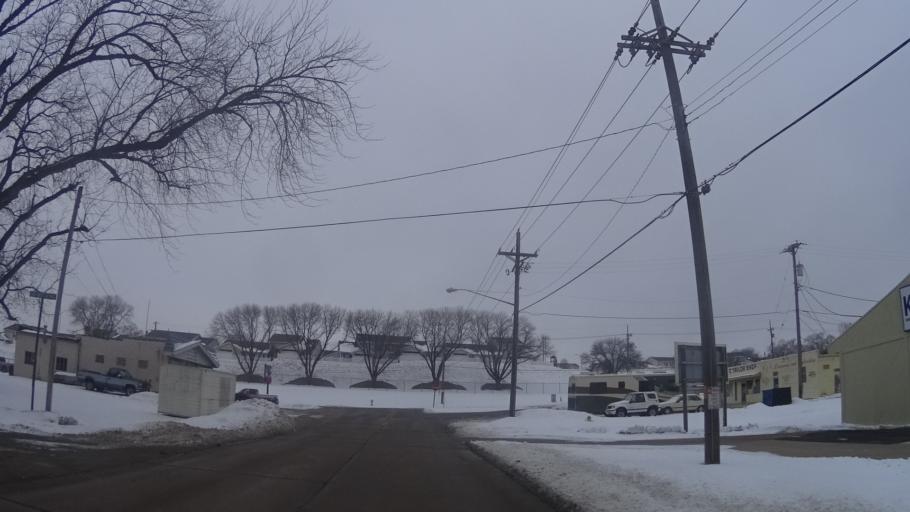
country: US
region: Nebraska
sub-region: Sarpy County
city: Bellevue
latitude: 41.1345
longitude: -95.9065
